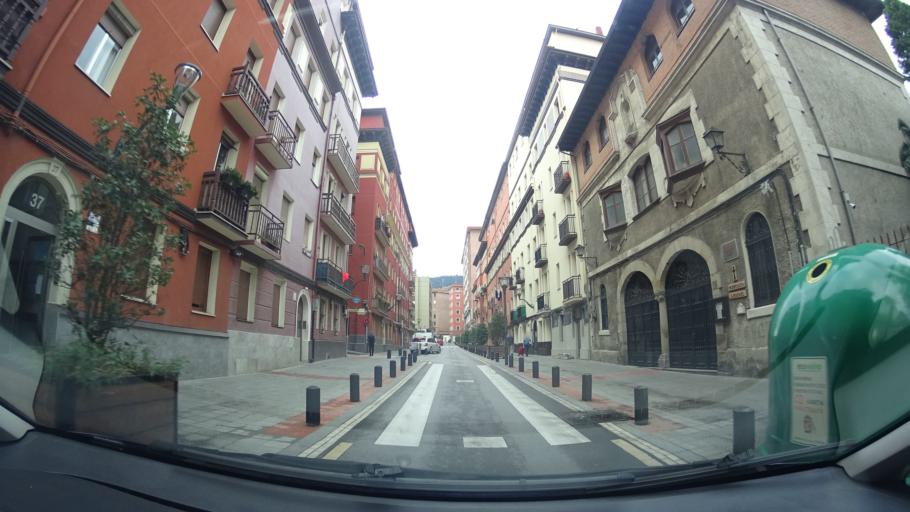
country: ES
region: Basque Country
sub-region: Bizkaia
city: Bilbao
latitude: 43.2540
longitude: -2.9323
